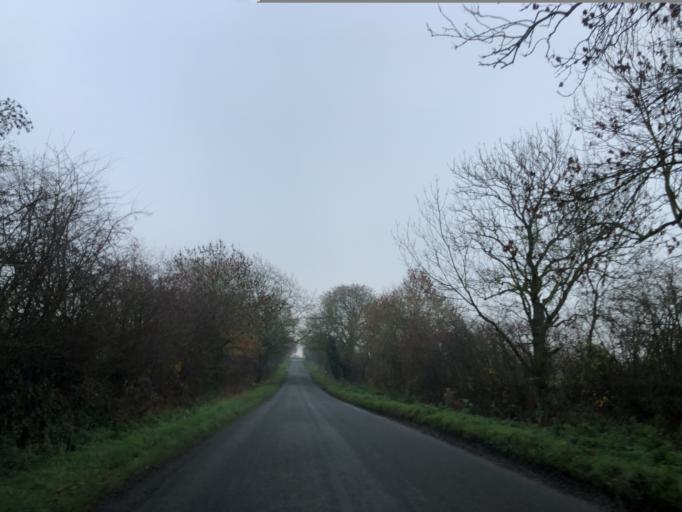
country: GB
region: England
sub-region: Solihull
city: Balsall Common
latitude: 52.3675
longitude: -1.6479
